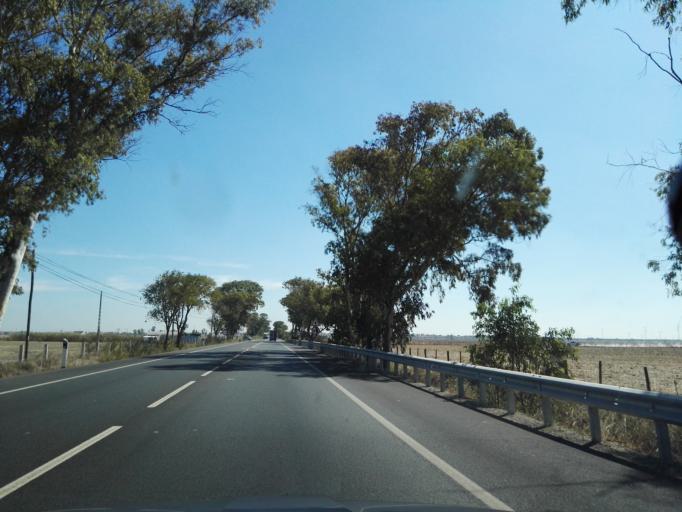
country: PT
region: Santarem
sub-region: Benavente
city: Samora Correia
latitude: 38.9338
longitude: -8.9194
